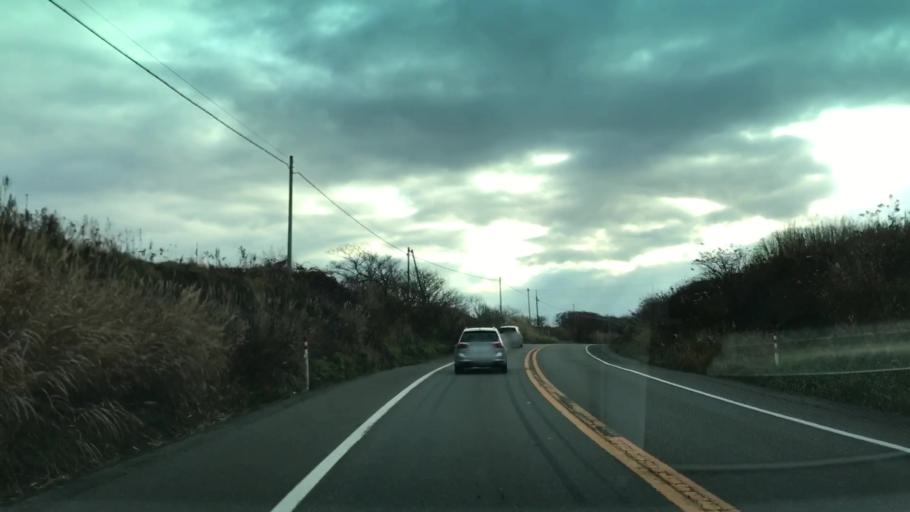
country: JP
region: Hokkaido
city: Shizunai-furukawacho
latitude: 42.4133
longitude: 142.2414
